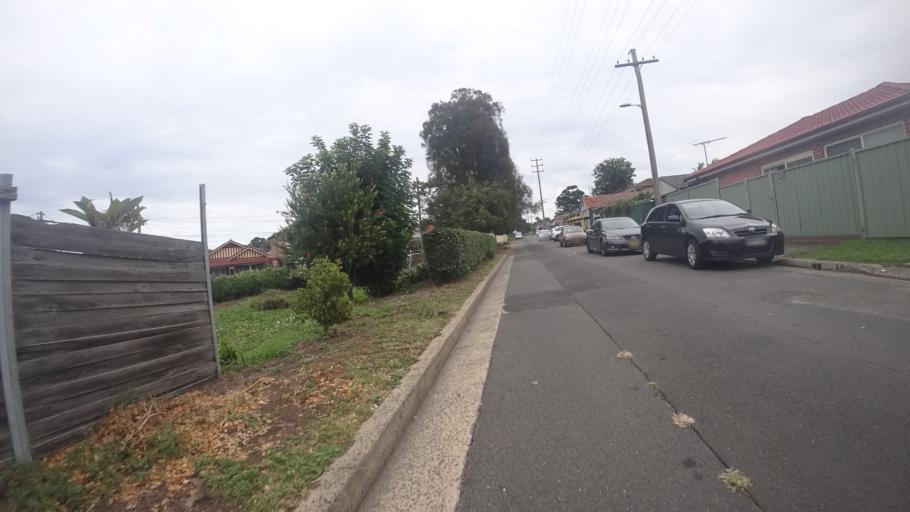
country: AU
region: New South Wales
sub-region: Rockdale
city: Bardwell Valley
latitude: -33.9372
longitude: 151.1363
